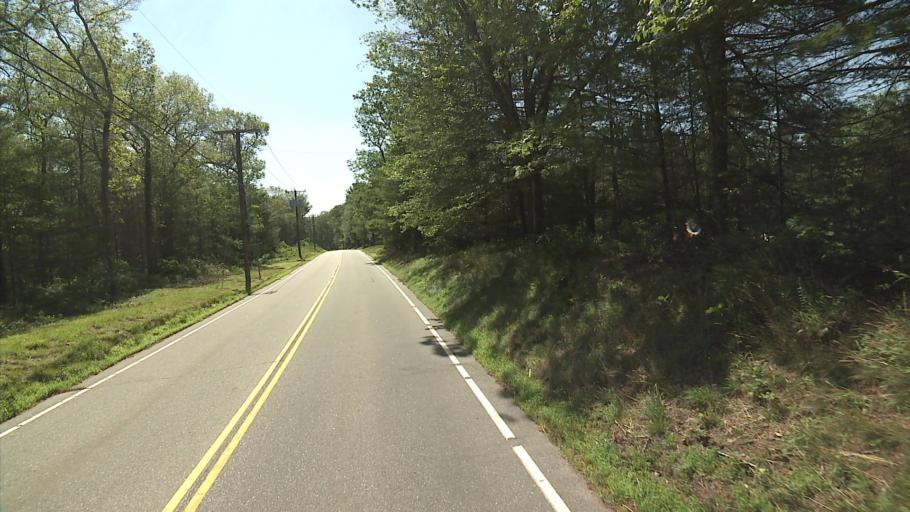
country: US
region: Connecticut
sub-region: Windham County
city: Moosup
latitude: 41.7090
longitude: -71.8410
